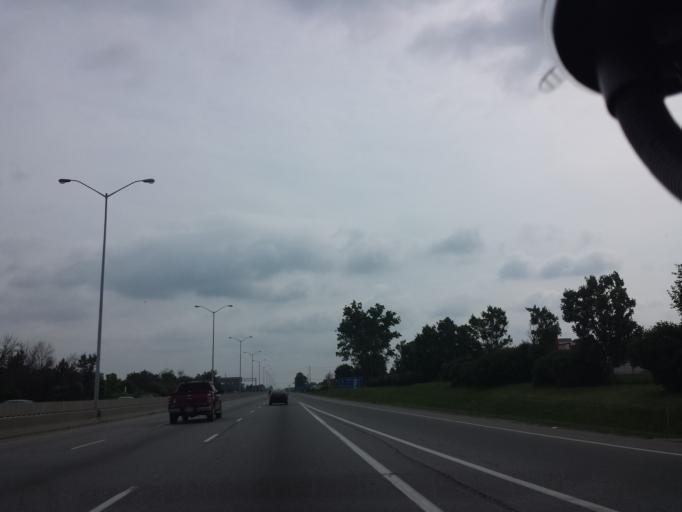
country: CA
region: Ontario
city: Bells Corners
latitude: 45.3517
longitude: -75.7856
